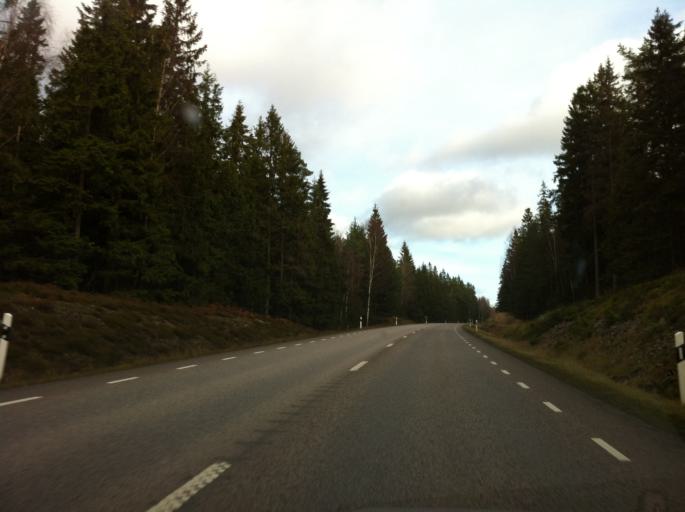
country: SE
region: Kronoberg
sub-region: Uppvidinge Kommun
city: Lenhovda
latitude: 57.0958
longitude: 15.1999
